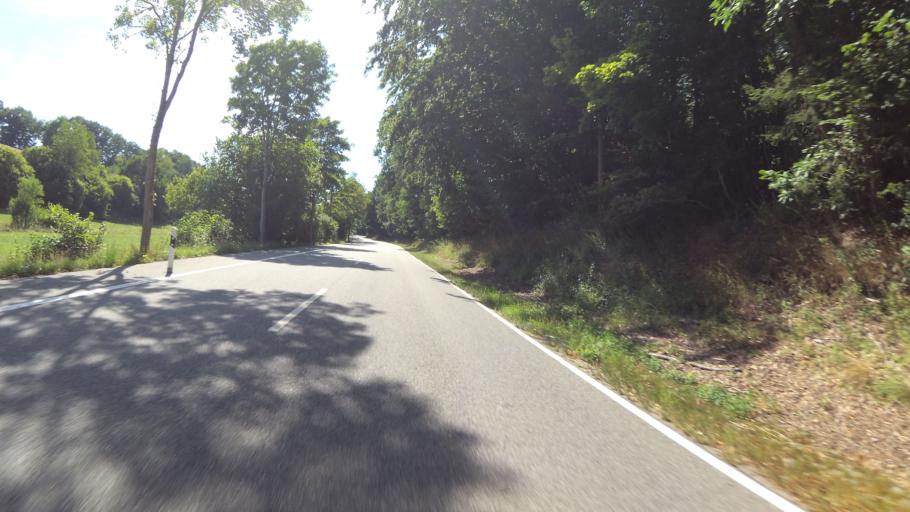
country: DE
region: Rheinland-Pfalz
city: Hornbach
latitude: 49.1514
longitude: 7.3555
